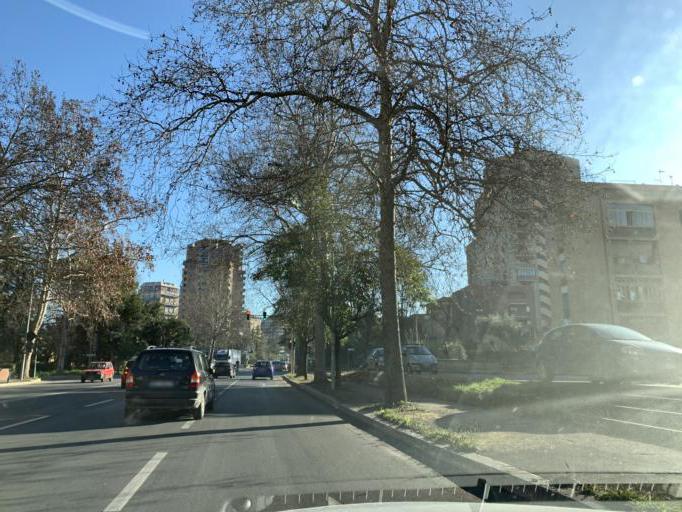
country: IT
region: Umbria
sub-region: Provincia di Terni
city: Terni
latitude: 42.5519
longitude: 12.6387
